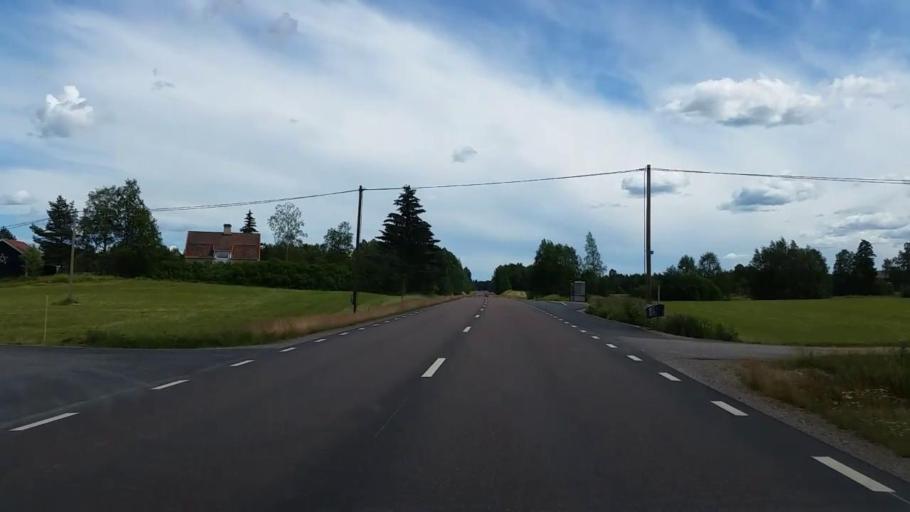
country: SE
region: Gaevleborg
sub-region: Ovanakers Kommun
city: Edsbyn
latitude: 61.3672
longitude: 15.8714
